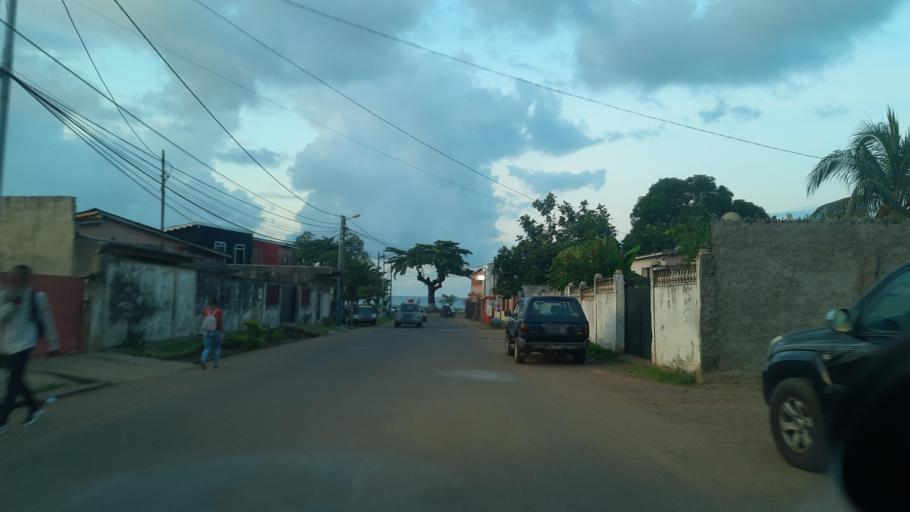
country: ST
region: Sao Tome Island
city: Sao Tome
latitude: 0.3338
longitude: 6.7384
